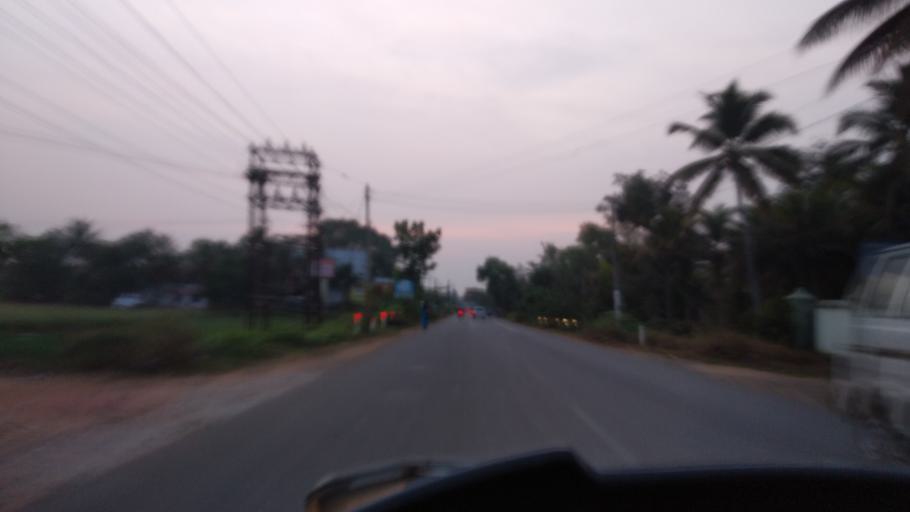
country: IN
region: Kerala
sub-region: Kottayam
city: Kottayam
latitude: 9.5921
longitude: 76.4462
